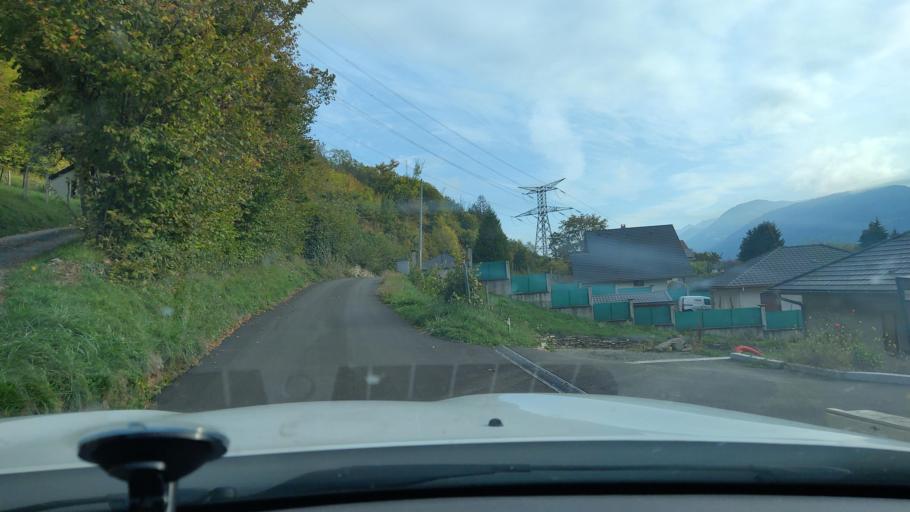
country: FR
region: Rhone-Alpes
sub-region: Departement de la Savoie
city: La Rochette
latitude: 45.4790
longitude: 6.1187
